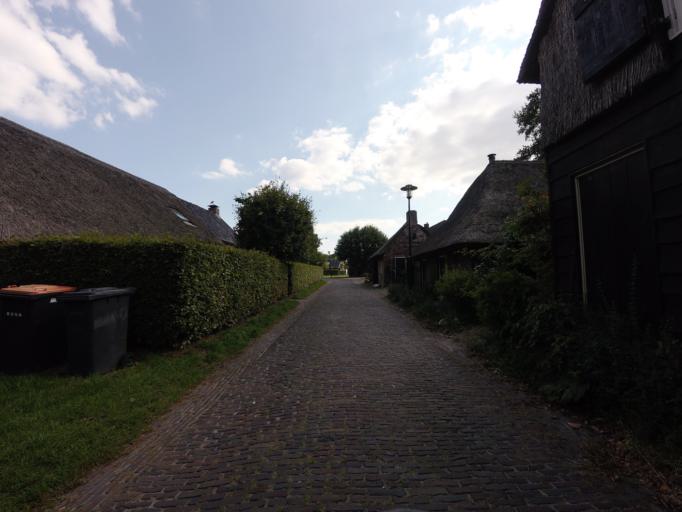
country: NL
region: Drenthe
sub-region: Gemeente Westerveld
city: Dwingeloo
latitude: 52.8341
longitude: 6.3717
